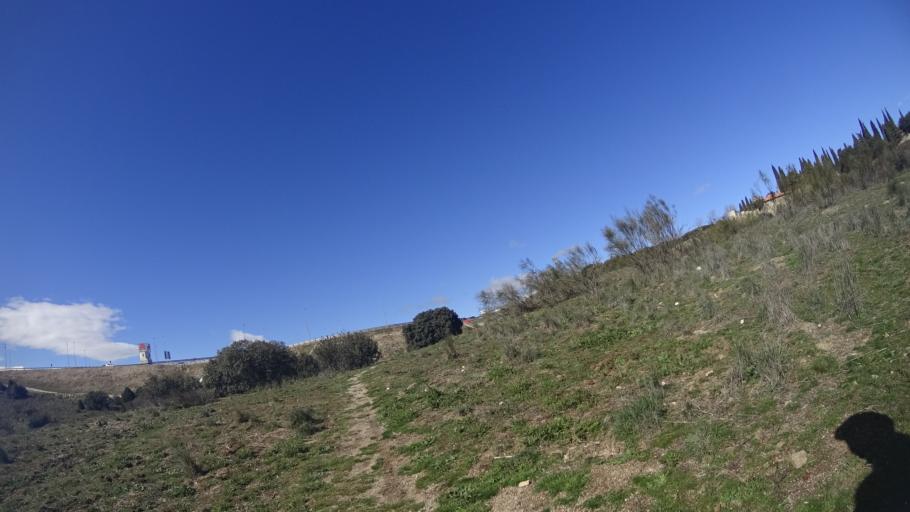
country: ES
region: Madrid
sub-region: Provincia de Madrid
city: Torrelodones
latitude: 40.5714
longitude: -3.9182
